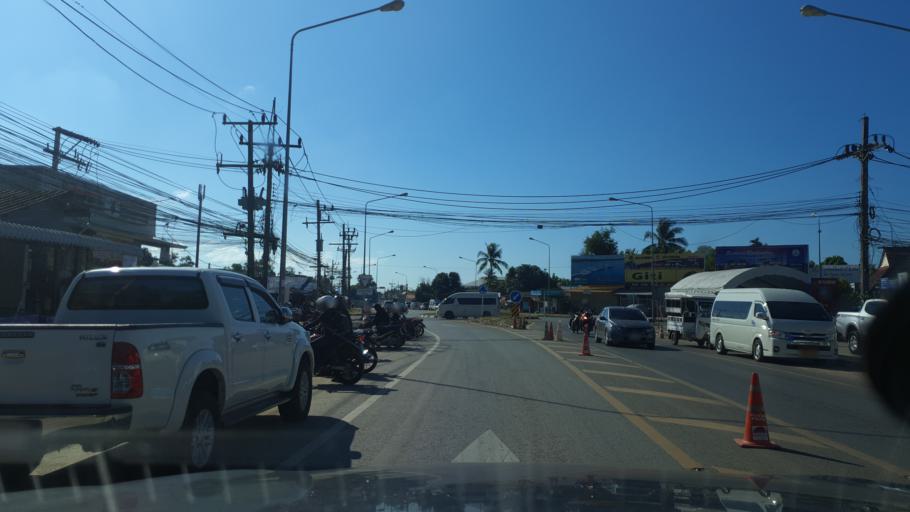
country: TH
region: Phangnga
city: Ban Ao Nang
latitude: 8.0335
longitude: 98.8616
